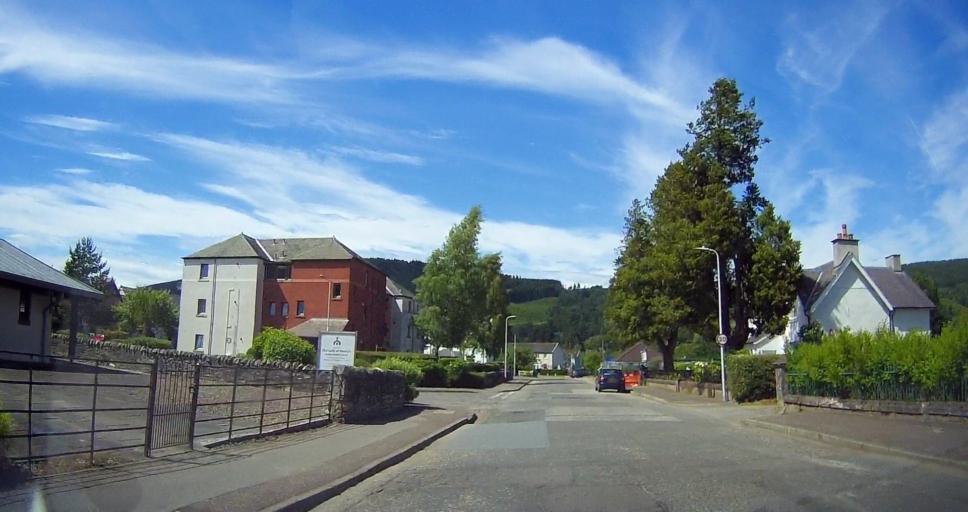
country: GB
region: Scotland
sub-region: Perth and Kinross
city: Aberfeldy
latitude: 56.6222
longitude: -3.8625
